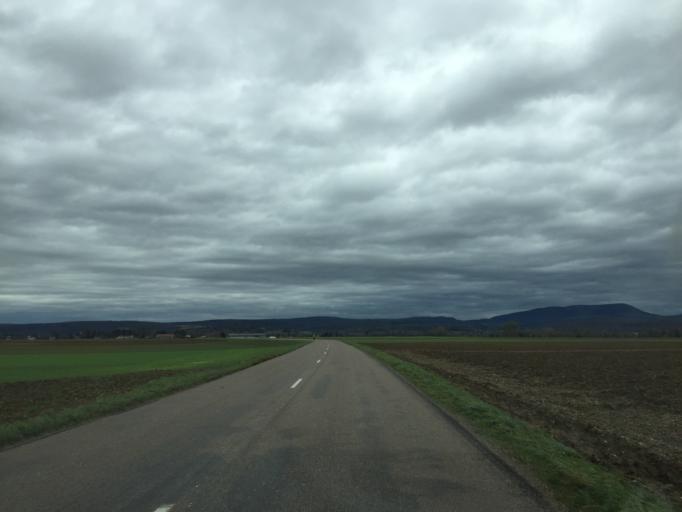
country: FR
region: Franche-Comte
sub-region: Departement du Doubs
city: Arc-et-Senans
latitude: 47.0276
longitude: 5.7431
